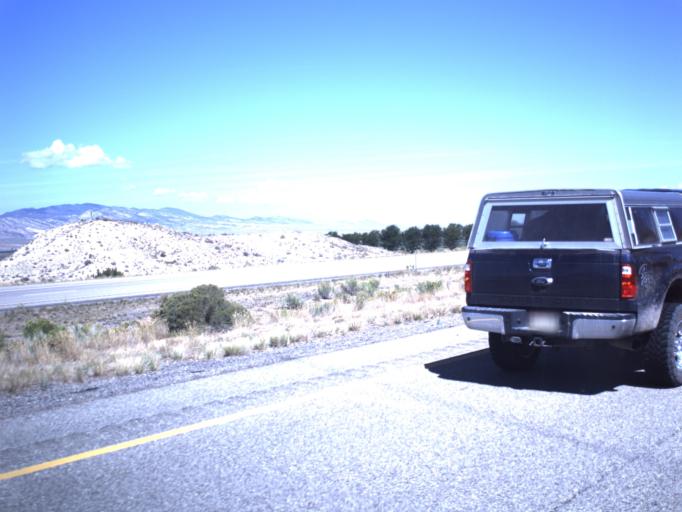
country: US
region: Utah
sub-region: Sevier County
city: Aurora
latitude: 38.9027
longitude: -111.9028
